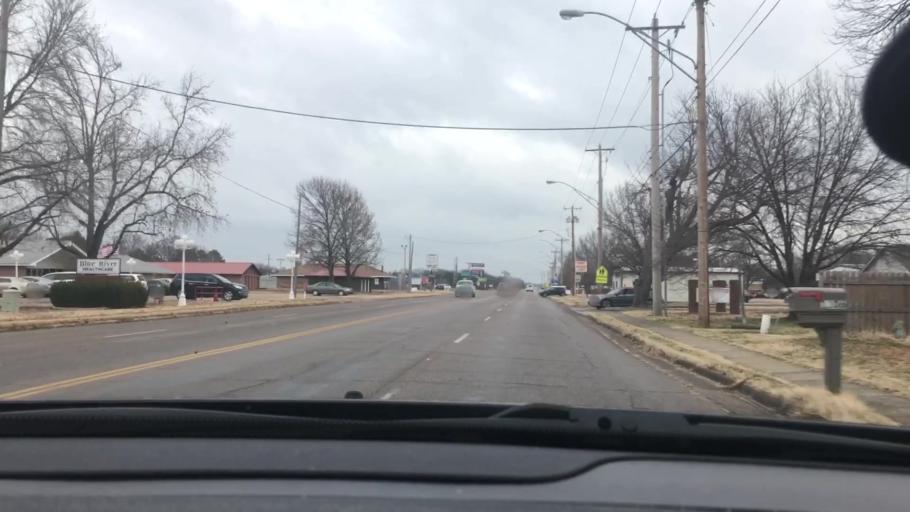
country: US
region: Oklahoma
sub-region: Johnston County
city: Tishomingo
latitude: 34.2305
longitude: -96.6653
